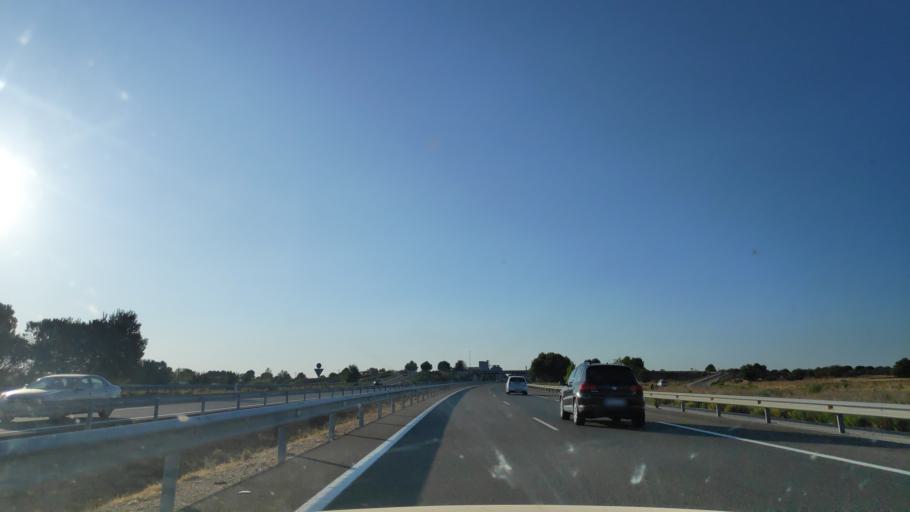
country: ES
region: Castille-La Mancha
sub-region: Provincia de Cuenca
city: Tarancon
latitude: 40.0018
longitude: -3.0244
